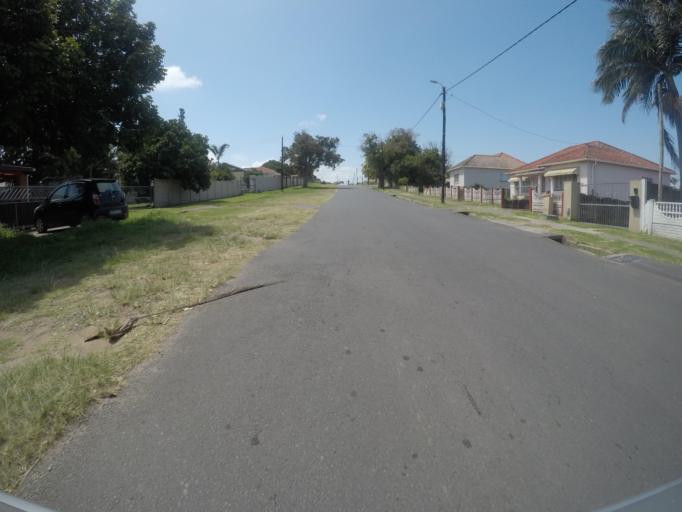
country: ZA
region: Eastern Cape
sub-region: Buffalo City Metropolitan Municipality
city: East London
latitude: -32.9733
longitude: 27.8710
